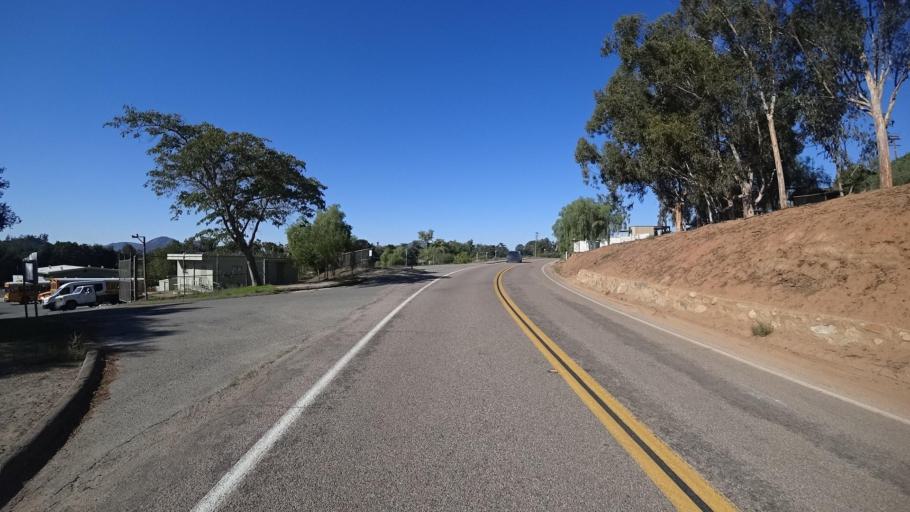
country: US
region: California
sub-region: San Diego County
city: Jamul
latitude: 32.7300
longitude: -116.8517
